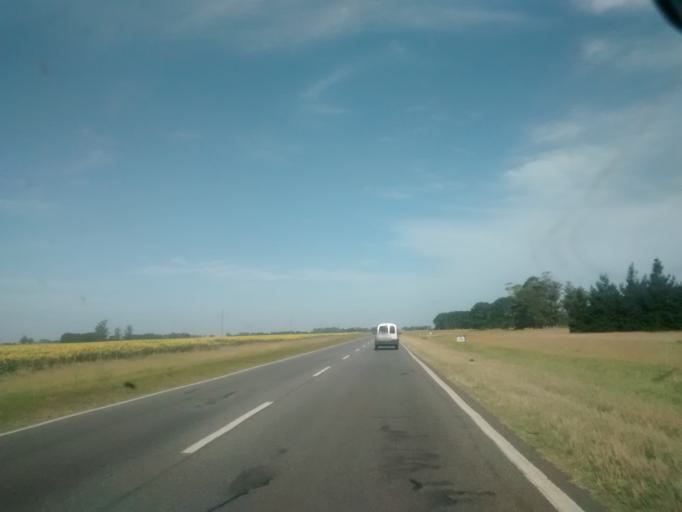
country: AR
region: Buenos Aires
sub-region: Partido de Balcarce
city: Balcarce
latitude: -37.6709
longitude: -58.4930
